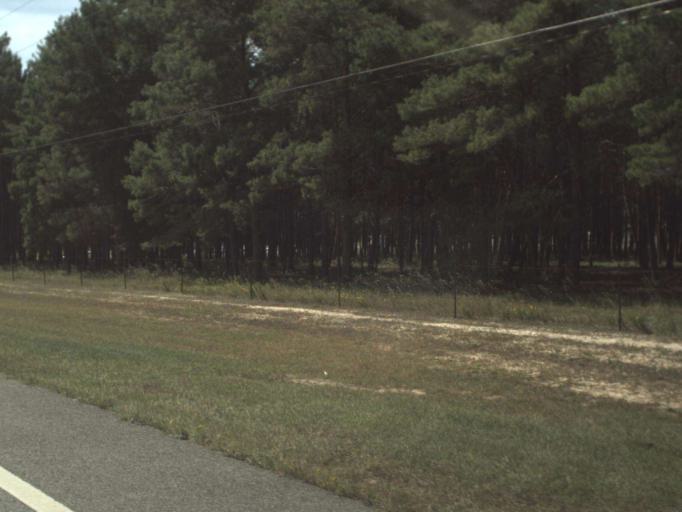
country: US
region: Florida
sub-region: Bay County
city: Youngstown
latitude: 30.5184
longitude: -85.6532
